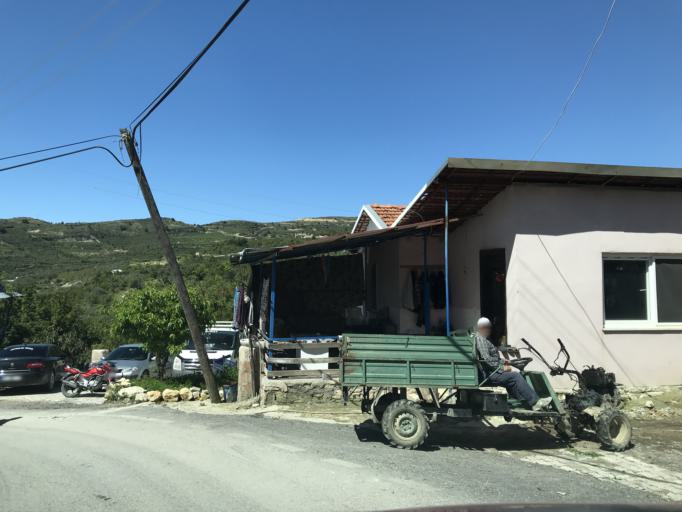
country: TR
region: Hatay
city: Samandag
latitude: 36.1353
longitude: 35.9758
